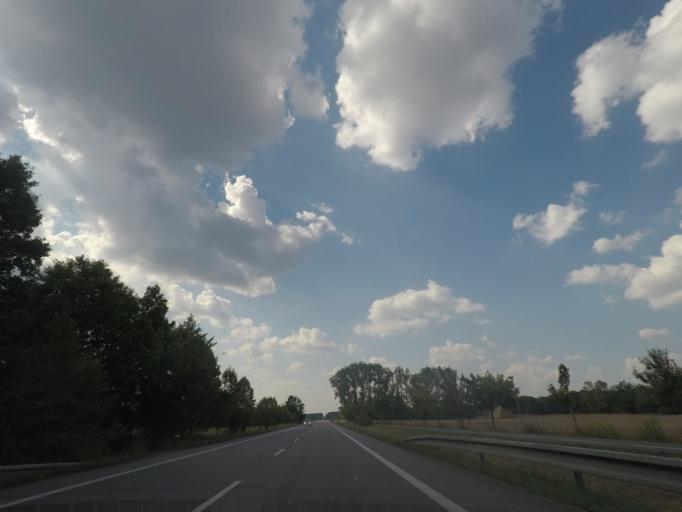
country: CZ
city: Albrechtice nad Orlici
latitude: 50.1646
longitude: 16.0510
